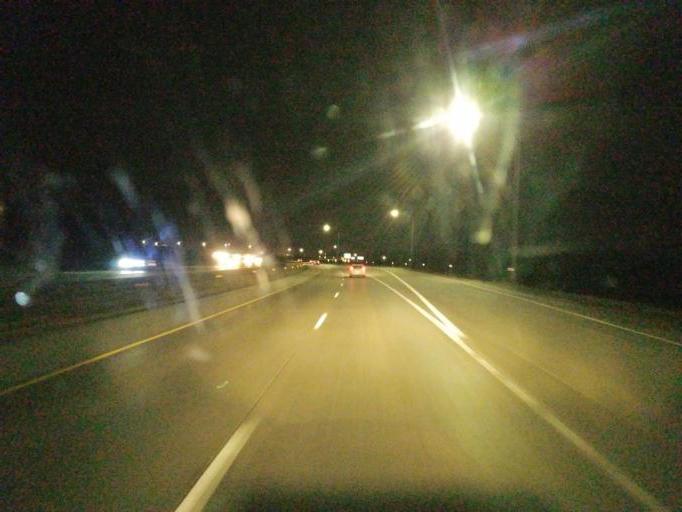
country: US
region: Iowa
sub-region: Dallas County
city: Waukee
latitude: 41.5656
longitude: -93.8619
